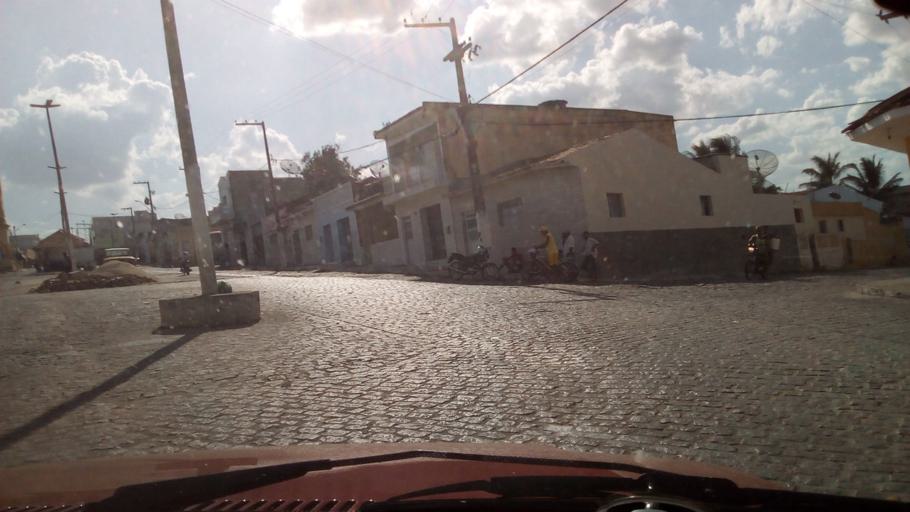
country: BR
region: Paraiba
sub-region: Arara
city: Arara
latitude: -6.8282
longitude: -35.7584
